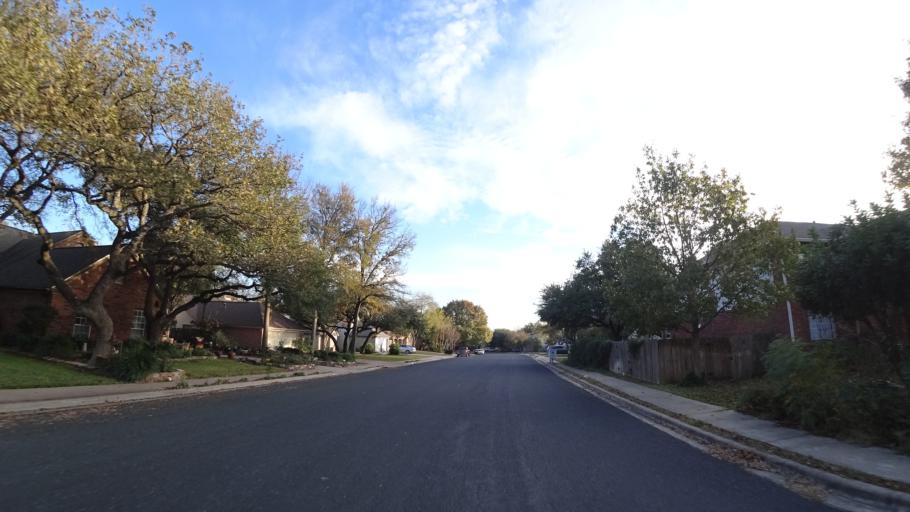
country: US
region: Texas
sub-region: Williamson County
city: Brushy Creek
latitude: 30.4926
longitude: -97.7415
